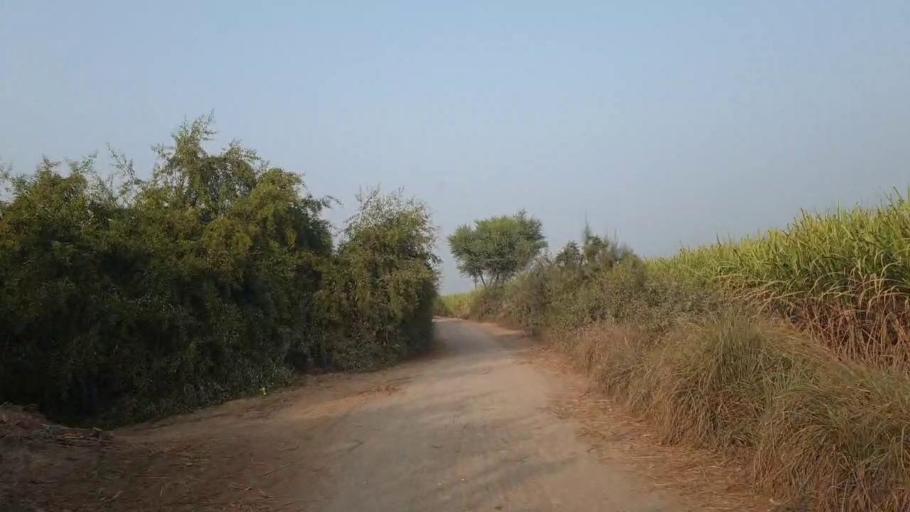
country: PK
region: Sindh
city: Shahdadpur
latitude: 25.8757
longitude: 68.6035
